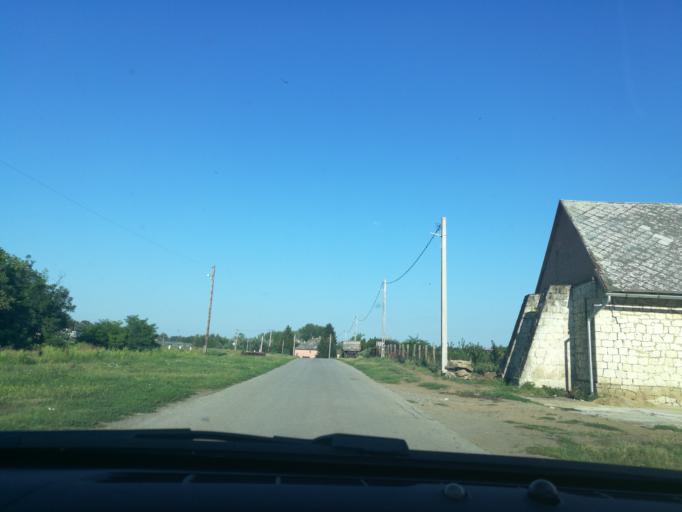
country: HU
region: Szabolcs-Szatmar-Bereg
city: Tiszabercel
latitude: 48.1686
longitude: 21.5764
